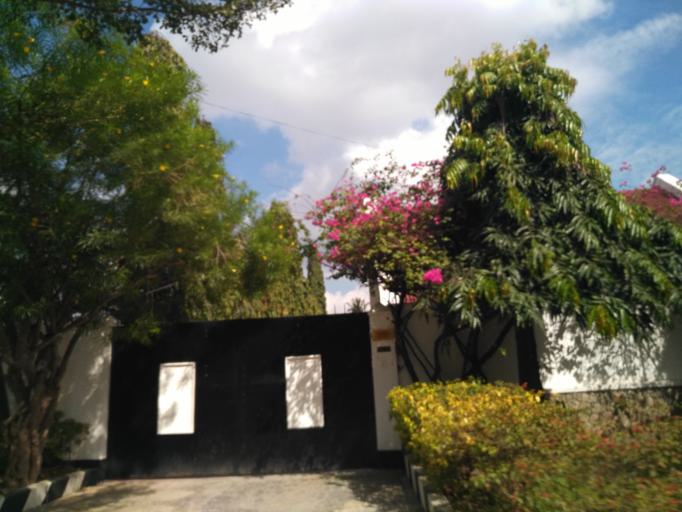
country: TZ
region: Dar es Salaam
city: Magomeni
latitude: -6.7624
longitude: 39.2466
